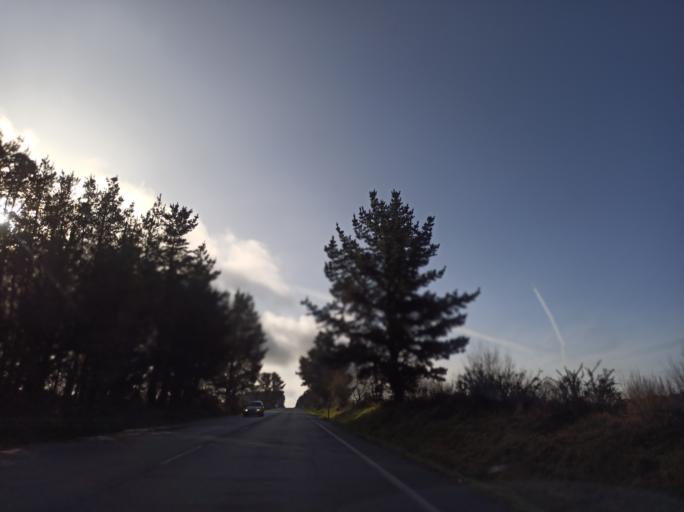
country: ES
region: Galicia
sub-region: Provincia da Coruna
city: Curtis
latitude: 43.1080
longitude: -8.0241
